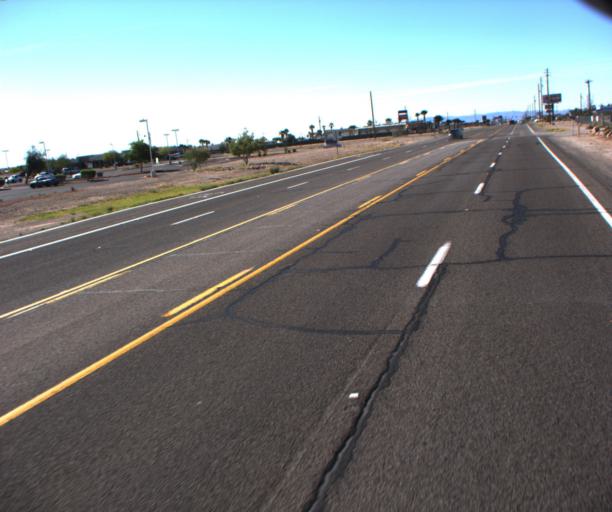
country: US
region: Arizona
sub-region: Mohave County
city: Mohave Valley
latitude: 35.0022
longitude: -114.5981
